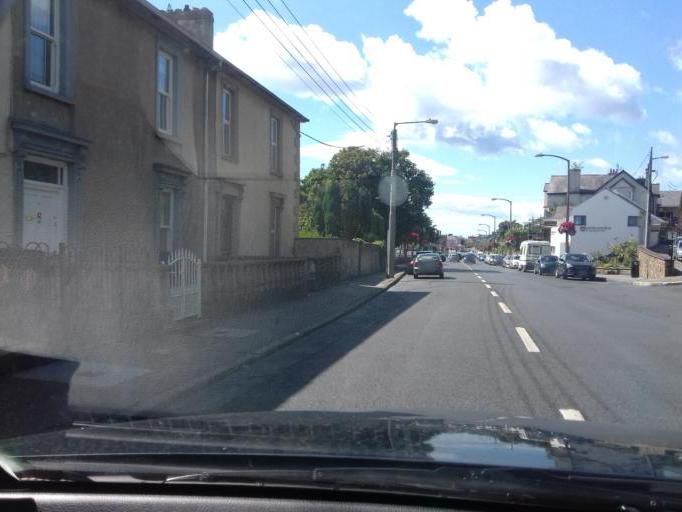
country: IE
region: Munster
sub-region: Waterford
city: Tra Mhor
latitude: 52.1651
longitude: -7.1462
